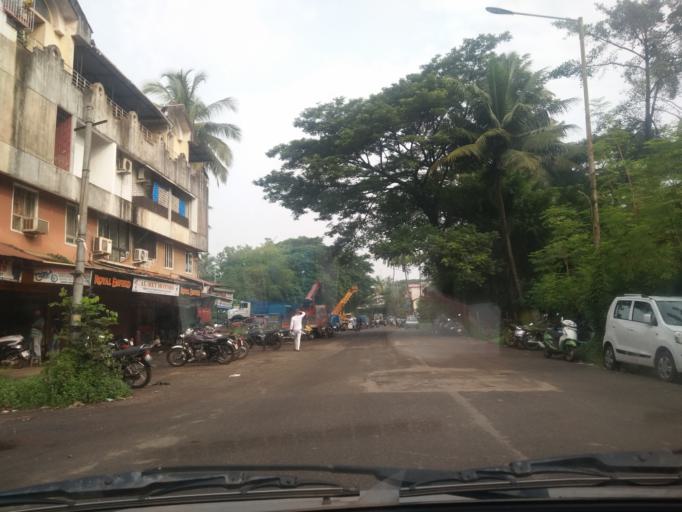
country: IN
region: Goa
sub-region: South Goa
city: Madgaon
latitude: 15.2661
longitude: 73.9605
